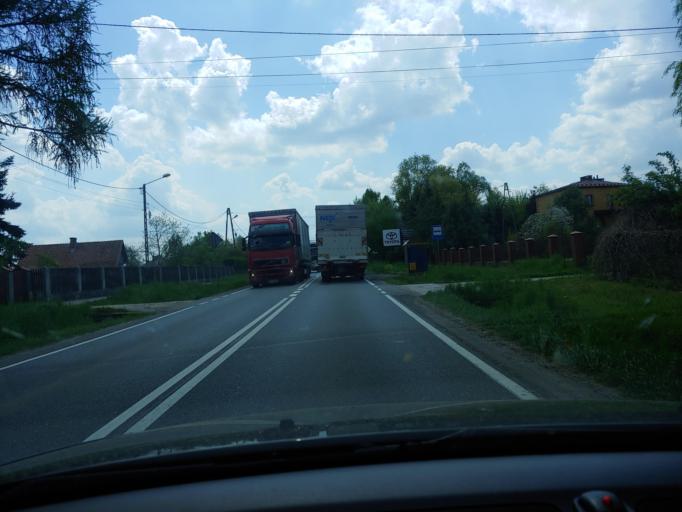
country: PL
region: Lesser Poland Voivodeship
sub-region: Powiat tarnowski
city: Lisia Gora
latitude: 50.0658
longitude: 21.0157
